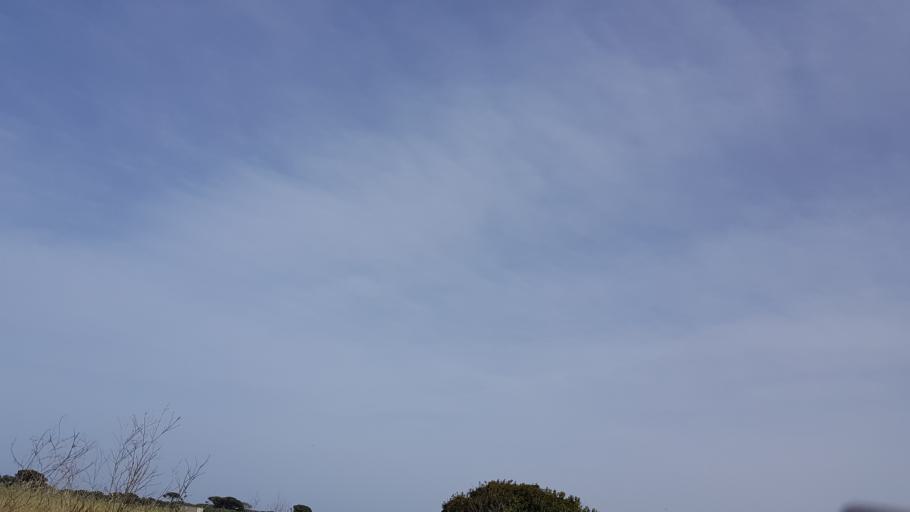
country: IT
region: Apulia
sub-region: Provincia di Brindisi
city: La Rosa
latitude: 40.5922
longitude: 17.9975
